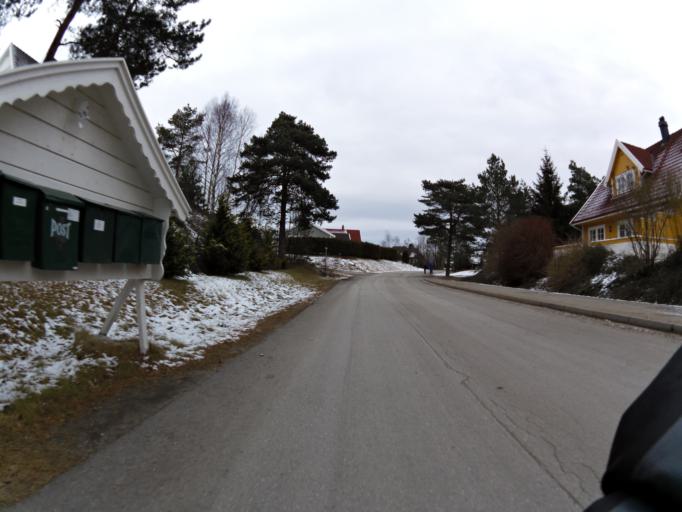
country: NO
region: Ostfold
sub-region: Fredrikstad
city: Fredrikstad
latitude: 59.1956
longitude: 10.8727
